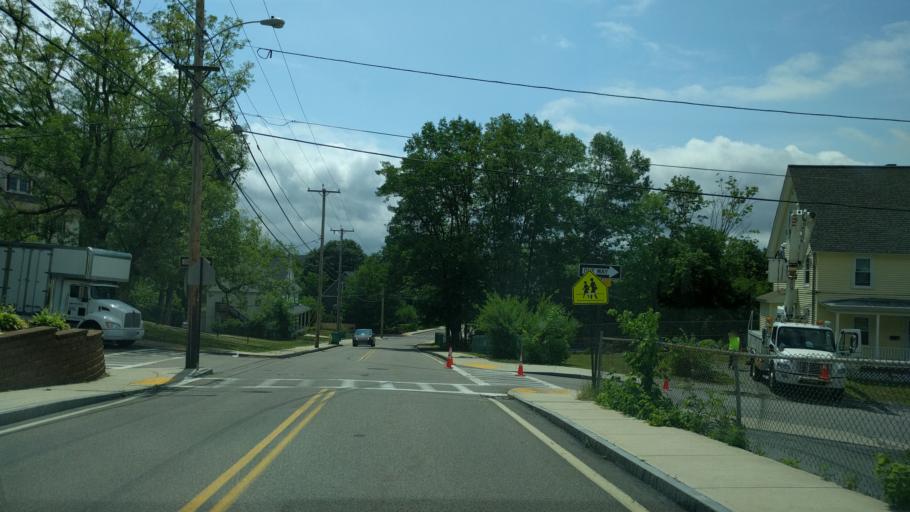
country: US
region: Massachusetts
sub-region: Worcester County
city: Whitinsville
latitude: 42.1153
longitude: -71.6825
